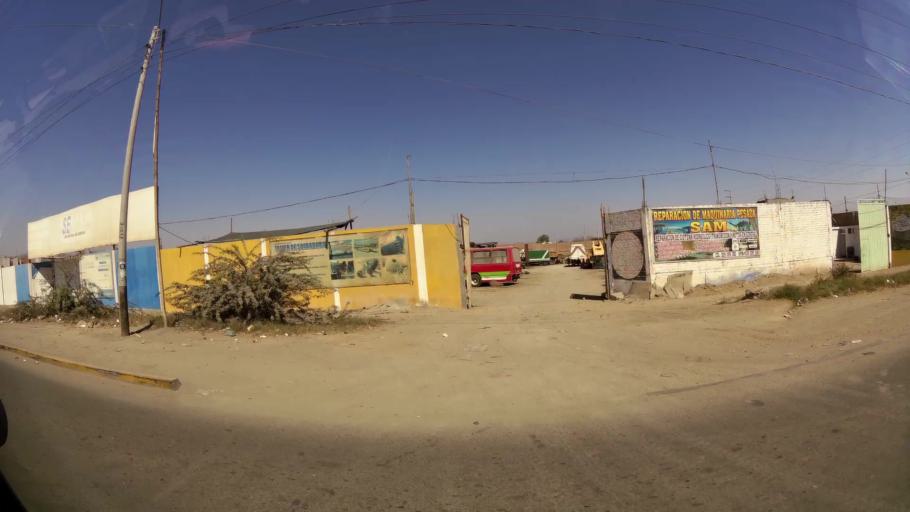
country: PE
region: Ica
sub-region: Provincia de Ica
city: Ica
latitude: -14.0591
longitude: -75.7132
